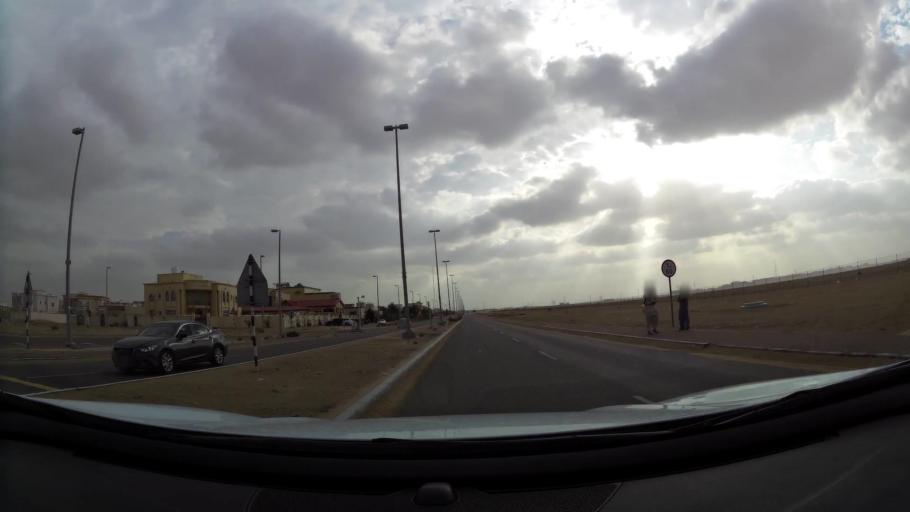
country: AE
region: Abu Dhabi
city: Abu Dhabi
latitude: 24.3556
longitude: 54.6119
